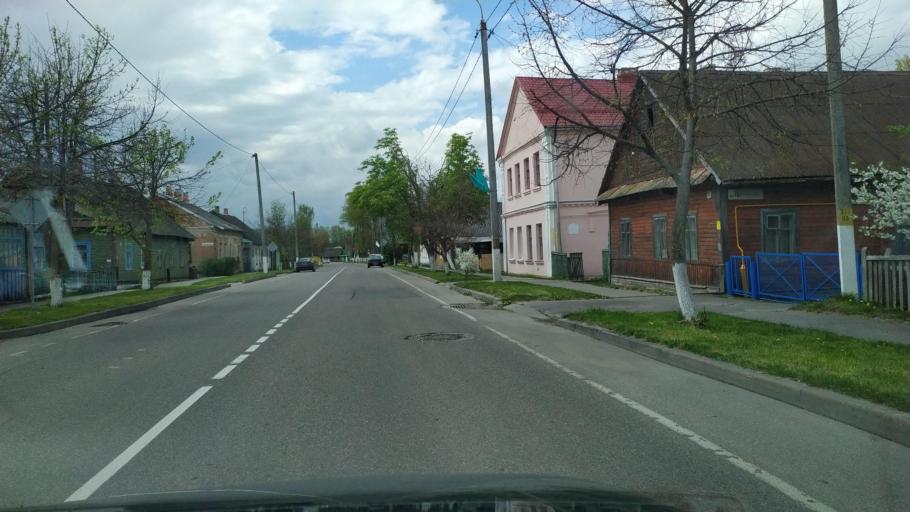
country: BY
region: Brest
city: Pruzhany
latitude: 52.5560
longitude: 24.4538
